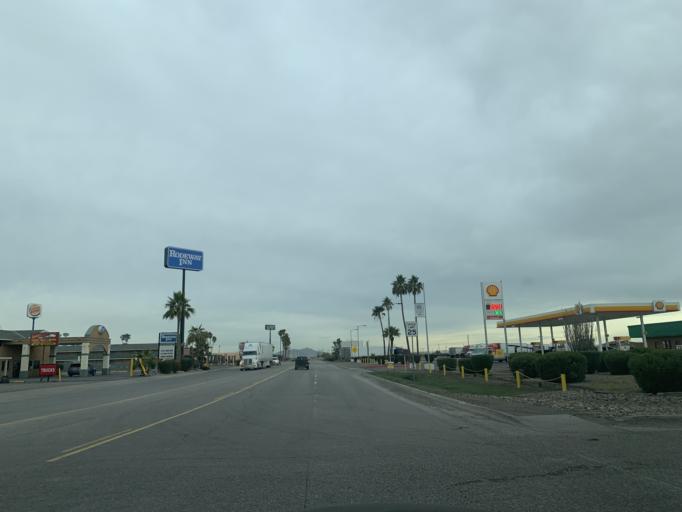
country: US
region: Arizona
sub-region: Pinal County
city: Arizona City
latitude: 32.8118
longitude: -111.6710
